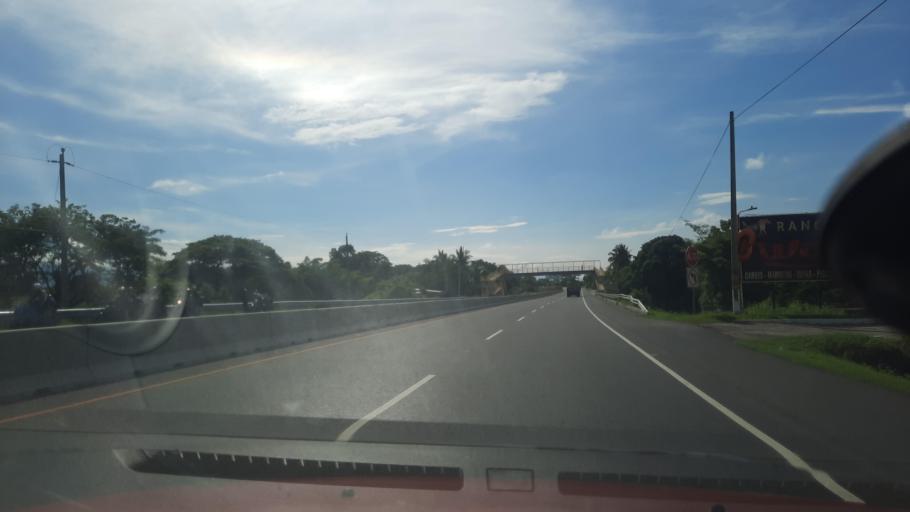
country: SV
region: La Paz
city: Santiago Nonualco
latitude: 13.4855
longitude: -88.9770
